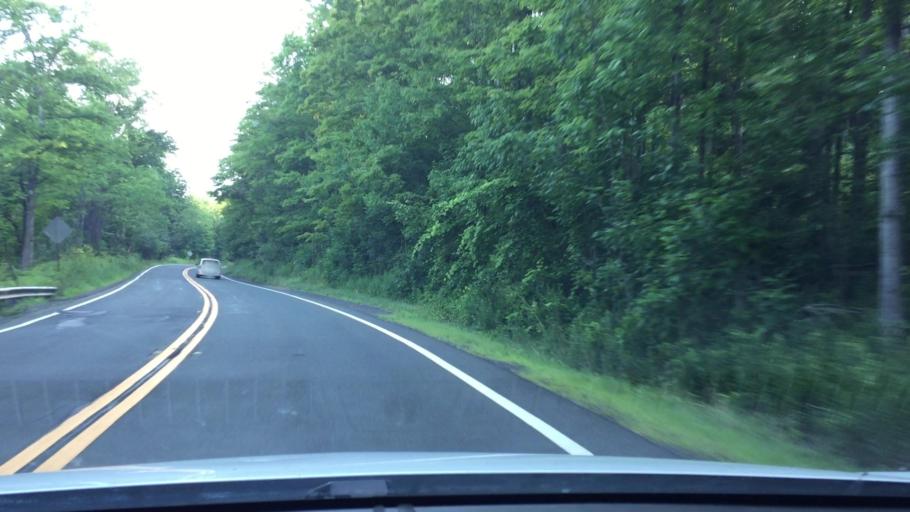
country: US
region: Massachusetts
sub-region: Berkshire County
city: Otis
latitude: 42.2271
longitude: -73.1079
